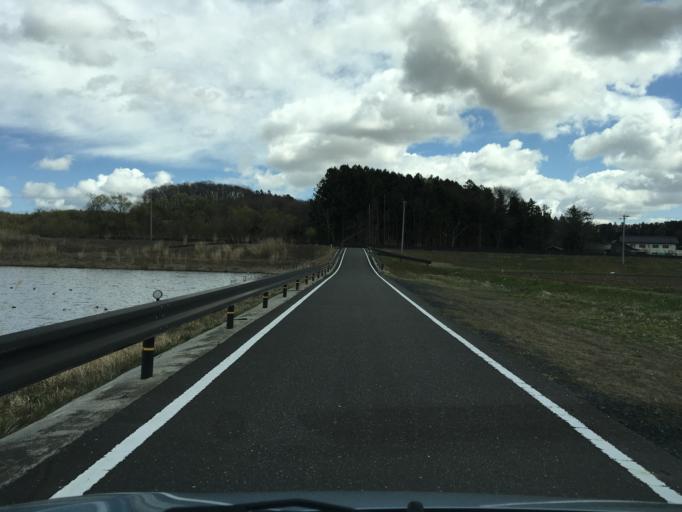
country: JP
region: Miyagi
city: Wakuya
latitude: 38.6813
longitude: 141.1026
